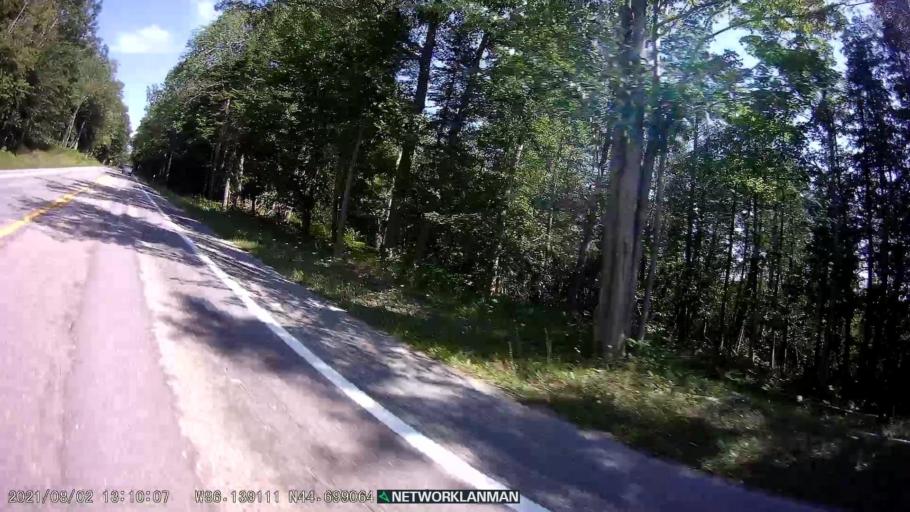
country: US
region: Michigan
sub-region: Benzie County
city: Beulah
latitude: 44.6994
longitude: -86.1385
